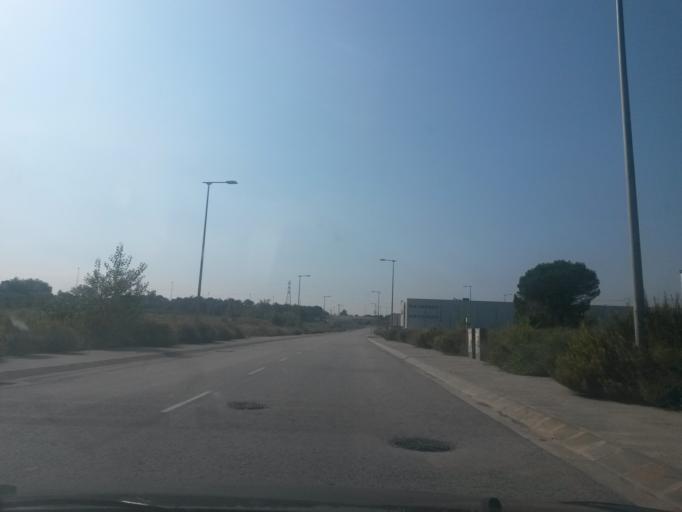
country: ES
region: Catalonia
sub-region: Provincia de Girona
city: Fornells de la Selva
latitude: 41.9441
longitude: 2.8041
